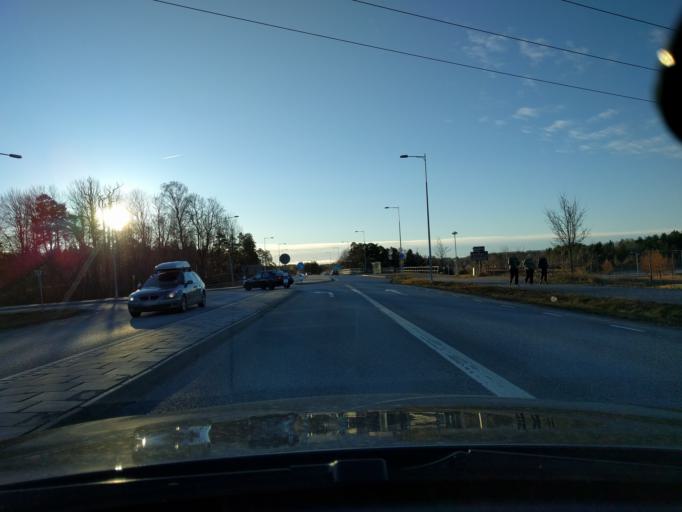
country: SE
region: Stockholm
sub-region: Taby Kommun
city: Taby
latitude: 59.4774
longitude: 18.0532
